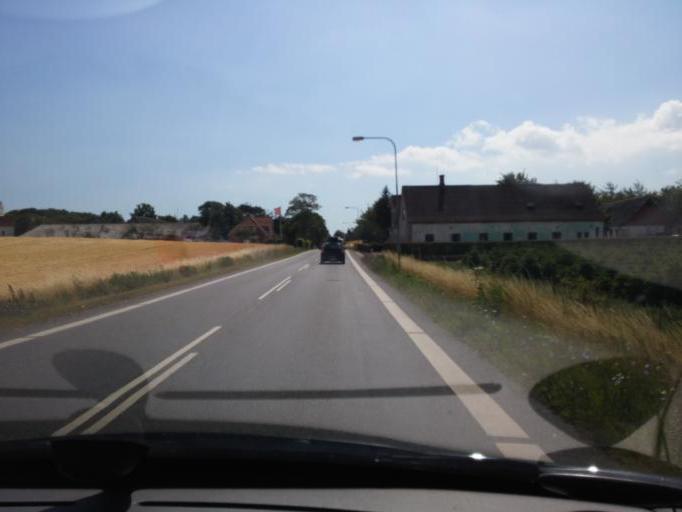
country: DK
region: South Denmark
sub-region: Langeland Kommune
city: Rudkobing
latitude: 54.8376
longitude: 10.7049
